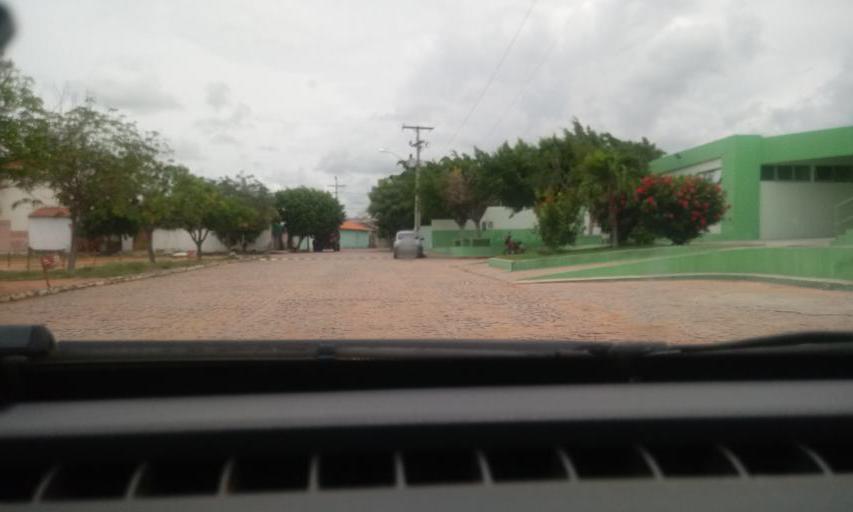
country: BR
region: Bahia
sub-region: Riacho De Santana
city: Riacho de Santana
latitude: -13.9105
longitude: -42.8435
